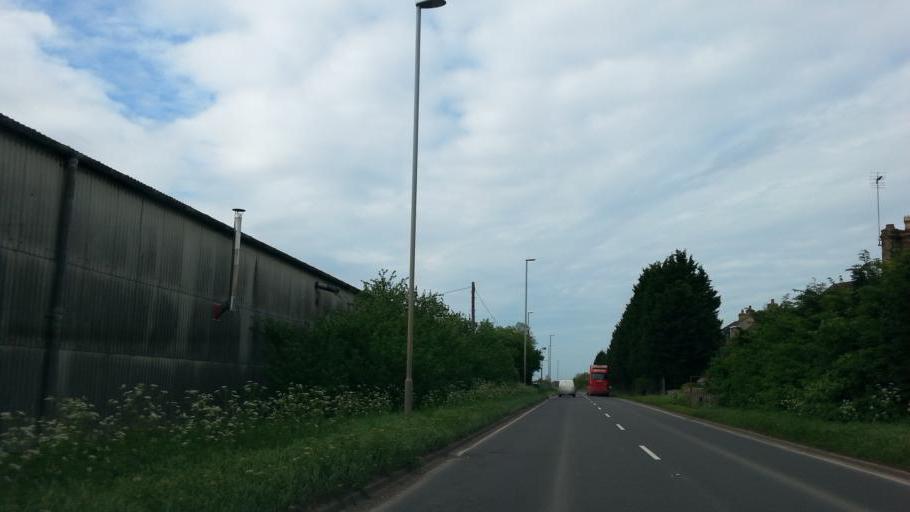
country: GB
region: England
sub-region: Cambridgeshire
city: Chatteris
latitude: 52.4532
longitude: 0.0396
